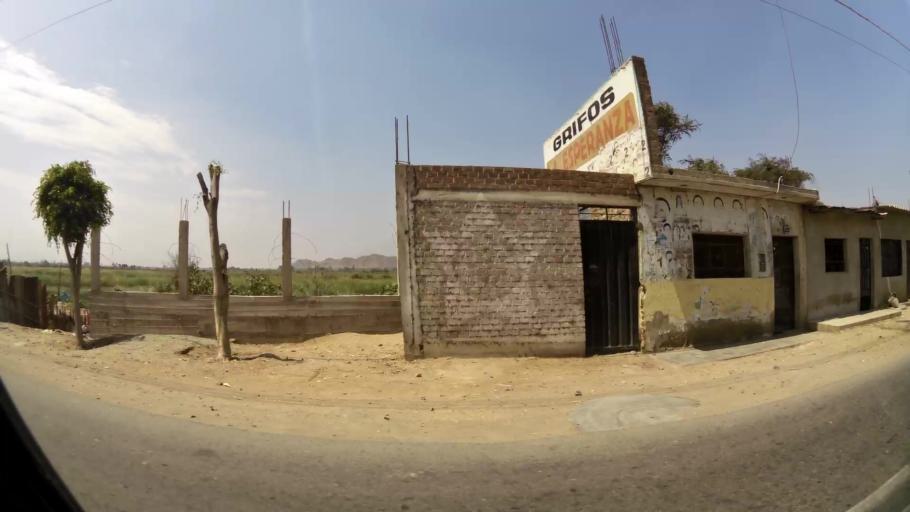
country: PE
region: La Libertad
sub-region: Chepen
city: Chepen
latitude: -7.2044
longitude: -79.4275
